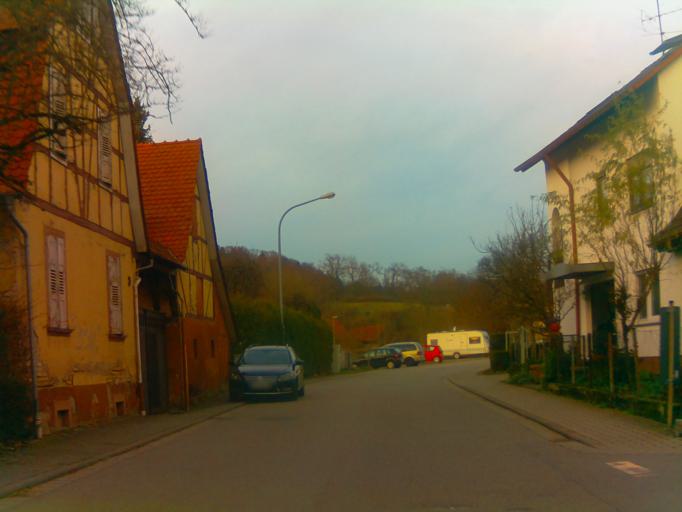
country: DE
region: Hesse
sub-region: Regierungsbezirk Darmstadt
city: Birkenau
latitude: 49.5795
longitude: 8.7216
